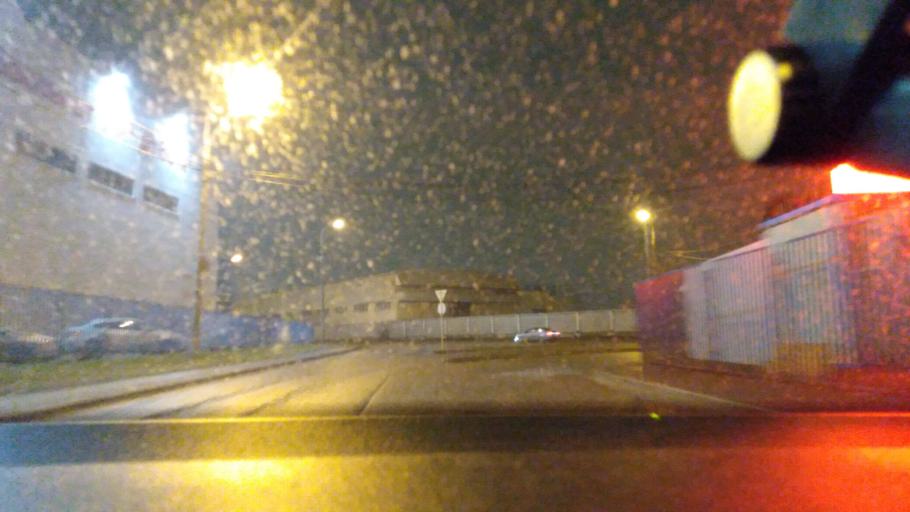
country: RU
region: Moskovskaya
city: Reutov
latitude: 55.7794
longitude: 37.8650
